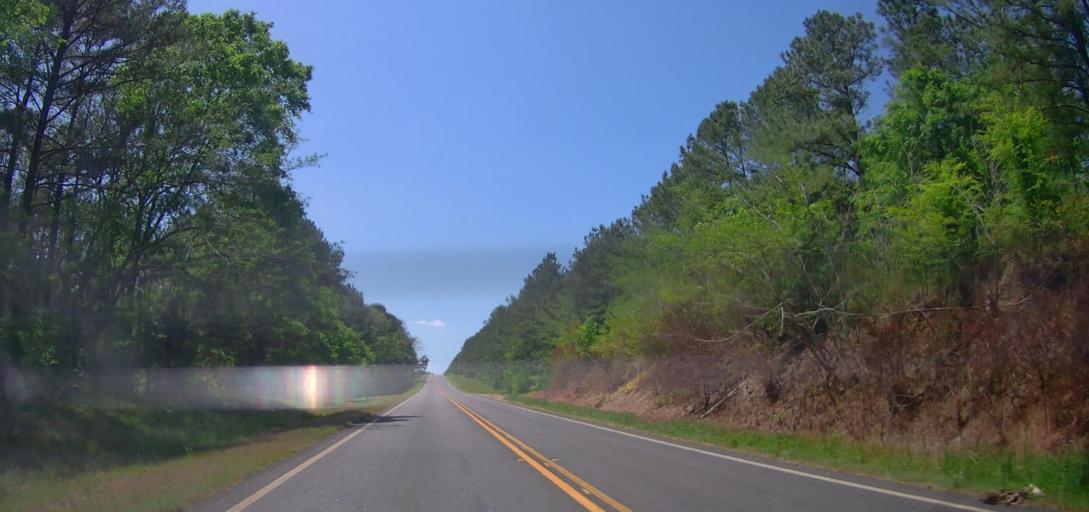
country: US
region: Georgia
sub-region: Putnam County
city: Eatonton
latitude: 33.2014
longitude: -83.4382
